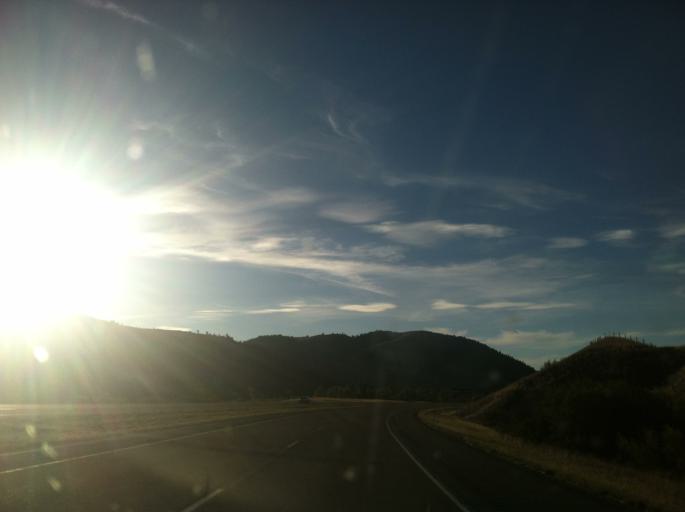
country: US
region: Montana
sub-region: Granite County
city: Philipsburg
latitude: 46.6809
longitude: -113.1886
